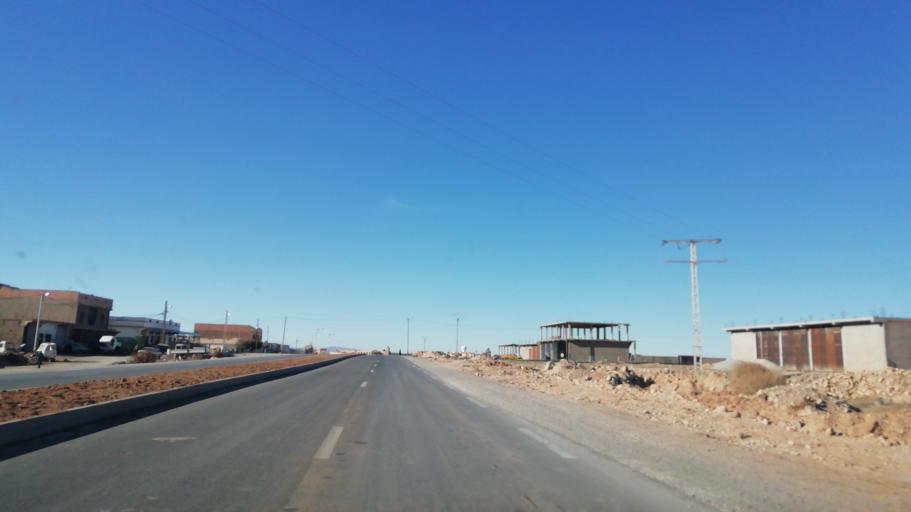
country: DZ
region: Tlemcen
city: Sebdou
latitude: 34.2194
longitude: -1.2486
